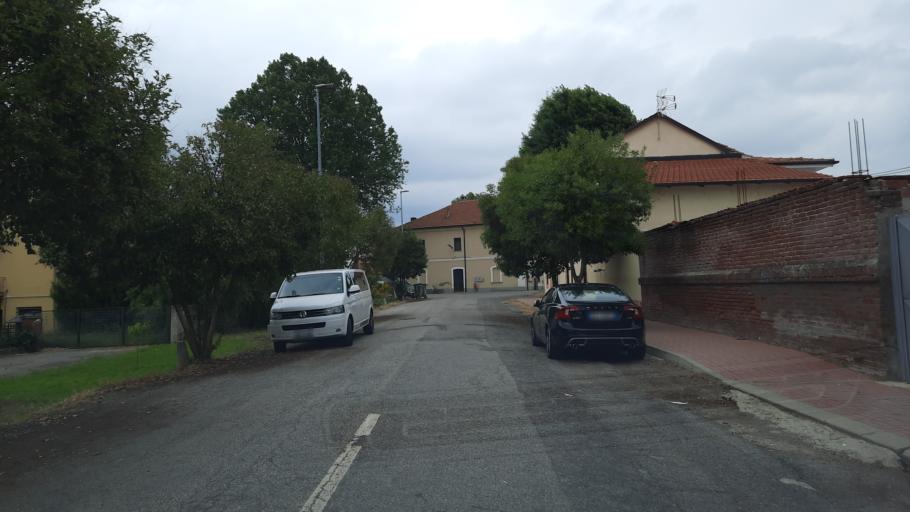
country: IT
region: Lombardy
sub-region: Provincia di Pavia
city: Palestro
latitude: 45.3064
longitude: 8.5341
